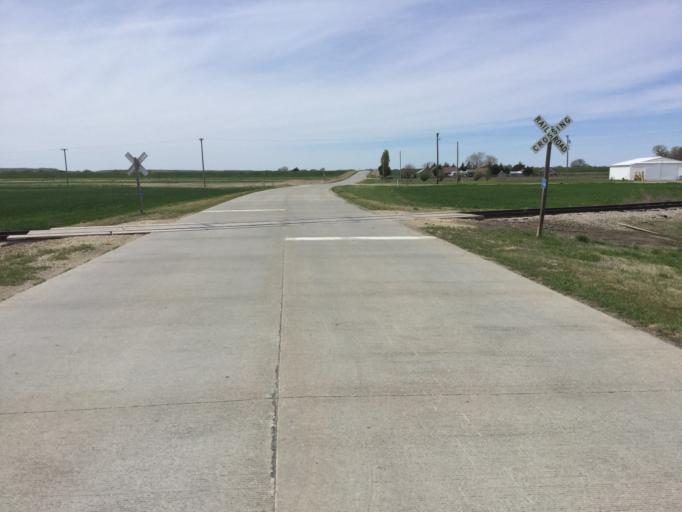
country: US
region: Kansas
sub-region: Osborne County
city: Osborne
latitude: 39.5021
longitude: -98.5521
